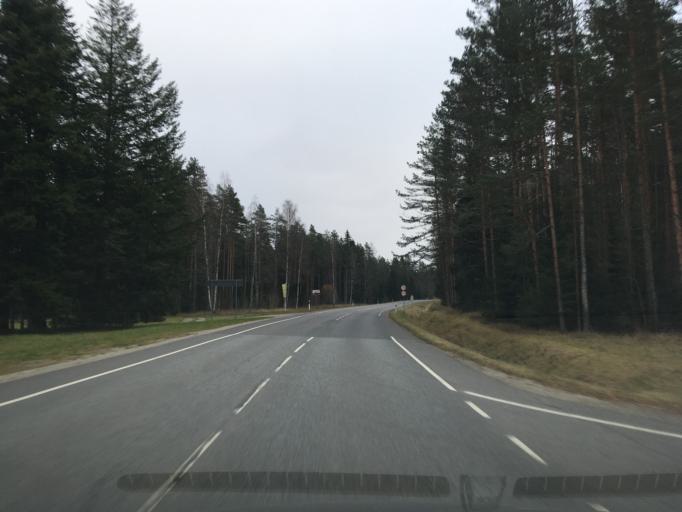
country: EE
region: Laeaene-Virumaa
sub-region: Kadrina vald
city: Kadrina
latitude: 59.4562
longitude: 26.0136
